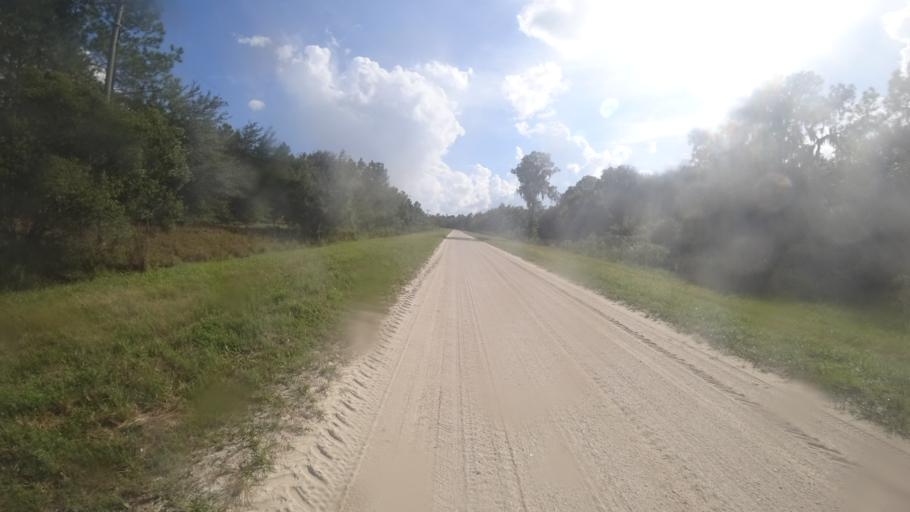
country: US
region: Florida
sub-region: Hillsborough County
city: Balm
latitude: 27.6095
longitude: -82.1197
